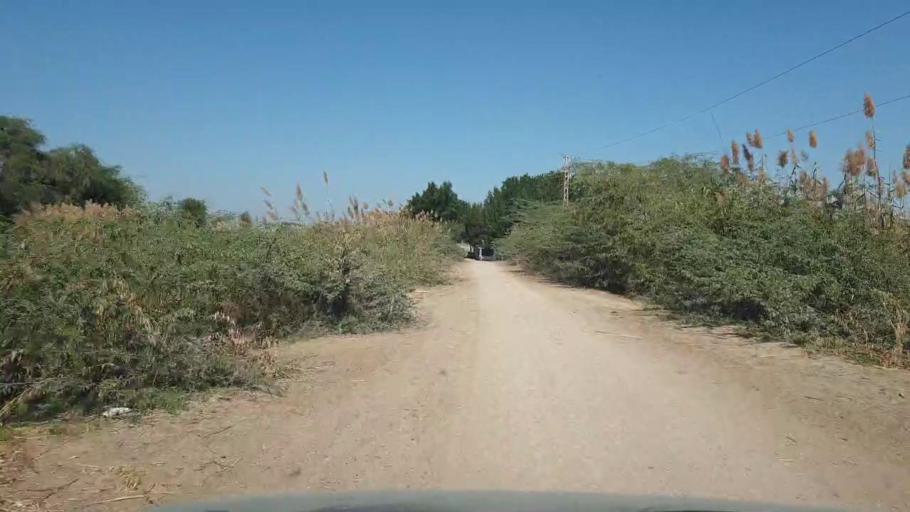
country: PK
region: Sindh
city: Mirwah Gorchani
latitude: 25.3185
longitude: 69.1278
